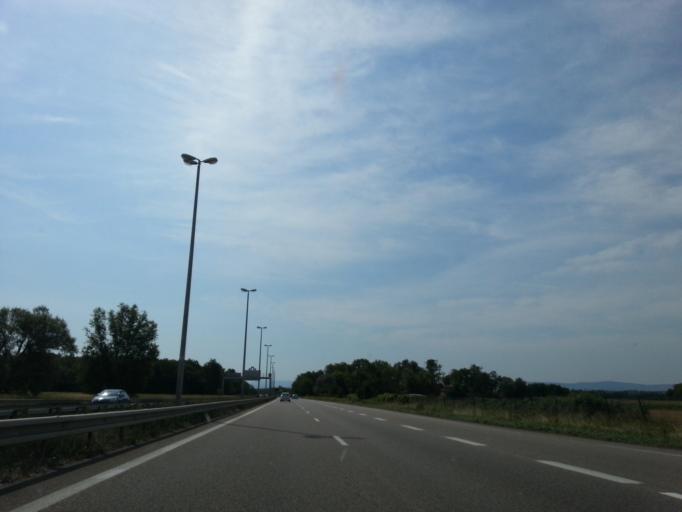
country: FR
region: Alsace
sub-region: Departement du Haut-Rhin
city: Bartenheim
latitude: 47.6342
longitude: 7.5017
